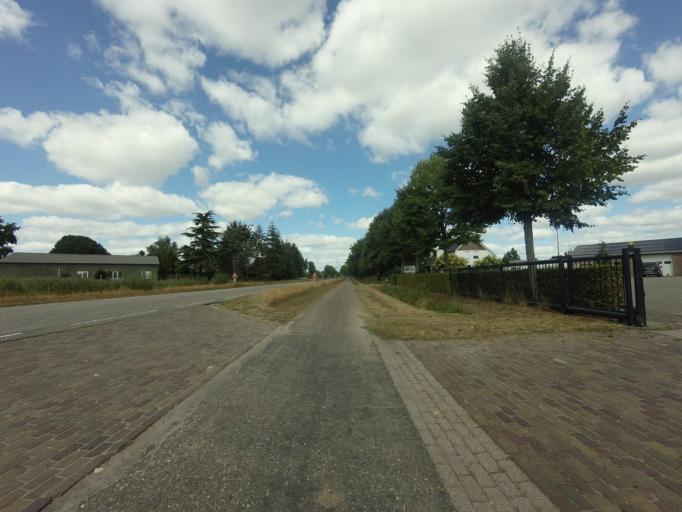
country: NL
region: North Brabant
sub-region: Gemeente Oss
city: Berghem
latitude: 51.7725
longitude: 5.5965
